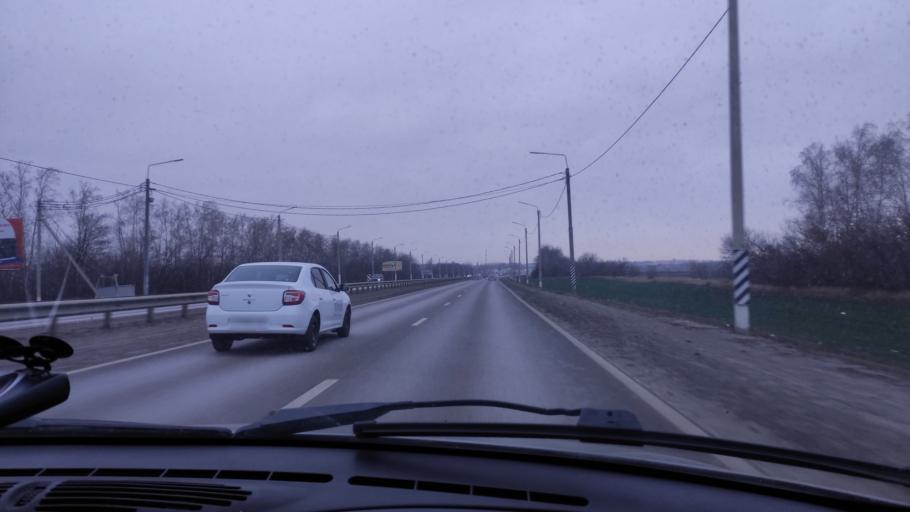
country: RU
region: Tambov
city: Komsomolets
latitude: 52.7260
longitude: 41.3450
